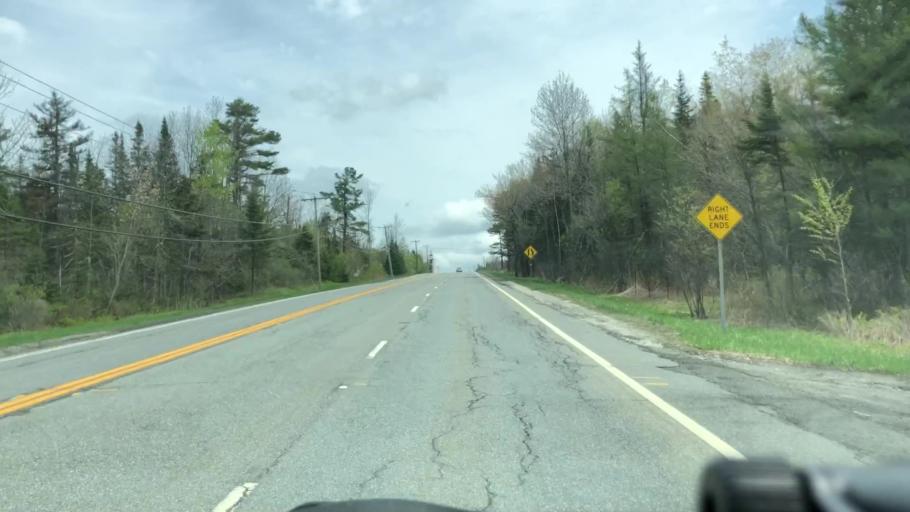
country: US
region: Massachusetts
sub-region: Berkshire County
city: Hinsdale
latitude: 42.5051
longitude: -73.0949
